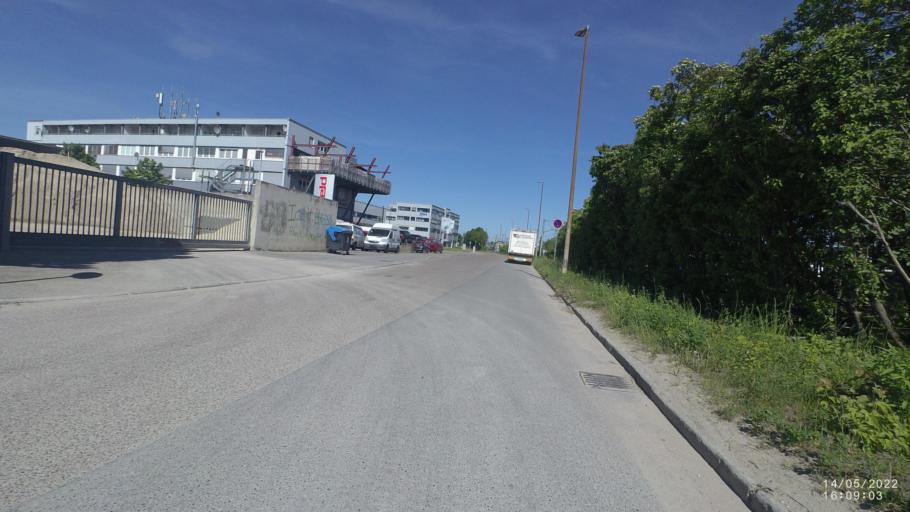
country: DE
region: Baden-Wuerttemberg
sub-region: Regierungsbezirk Stuttgart
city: Fellbach
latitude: 48.8183
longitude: 9.2630
